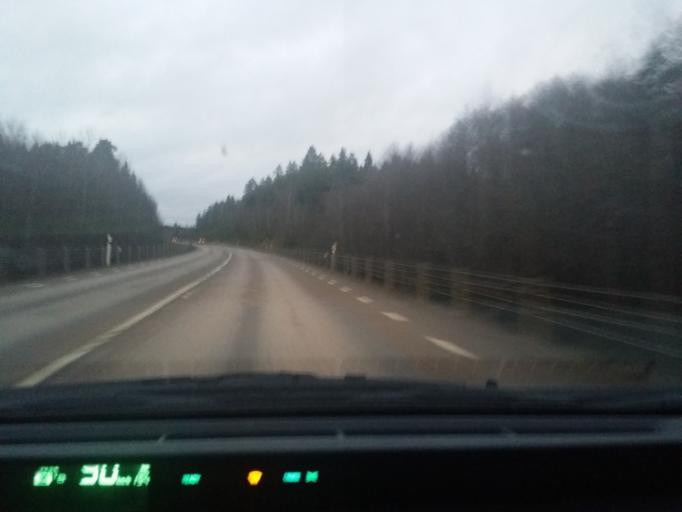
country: SE
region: Soedermanland
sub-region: Eskilstuna Kommun
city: Kvicksund
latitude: 59.5171
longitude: 16.3214
